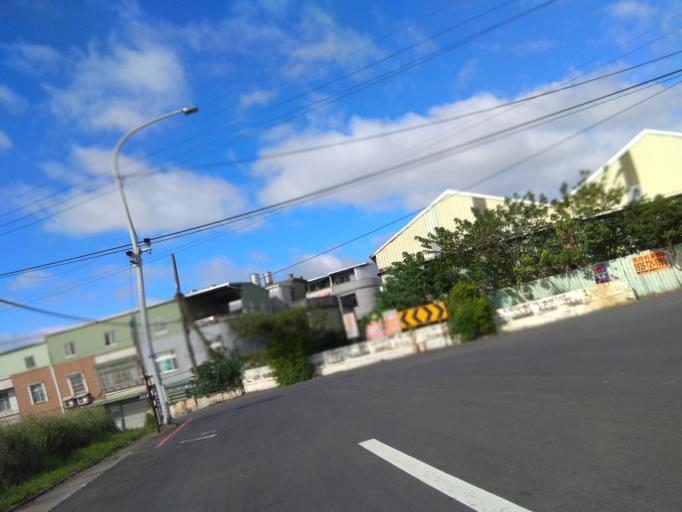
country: TW
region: Taiwan
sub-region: Hsinchu
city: Zhubei
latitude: 24.9730
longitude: 121.0966
